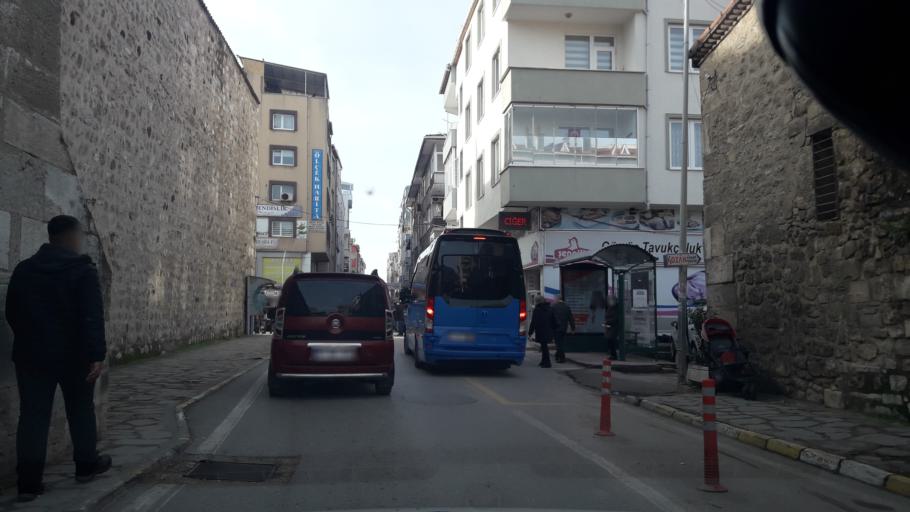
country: TR
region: Sinop
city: Sinop
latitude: 42.0269
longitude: 35.1482
